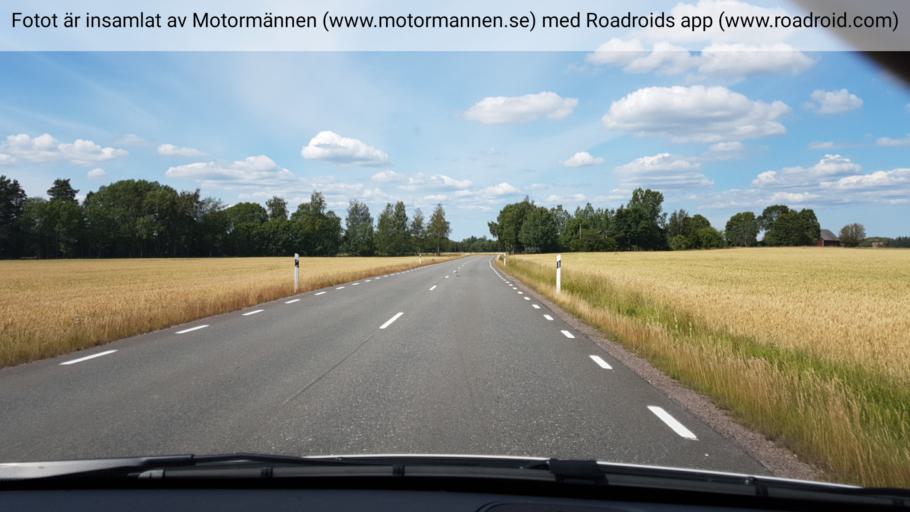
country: SE
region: Vaestra Goetaland
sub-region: Toreboda Kommun
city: Toereboda
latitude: 58.5920
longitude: 14.0785
